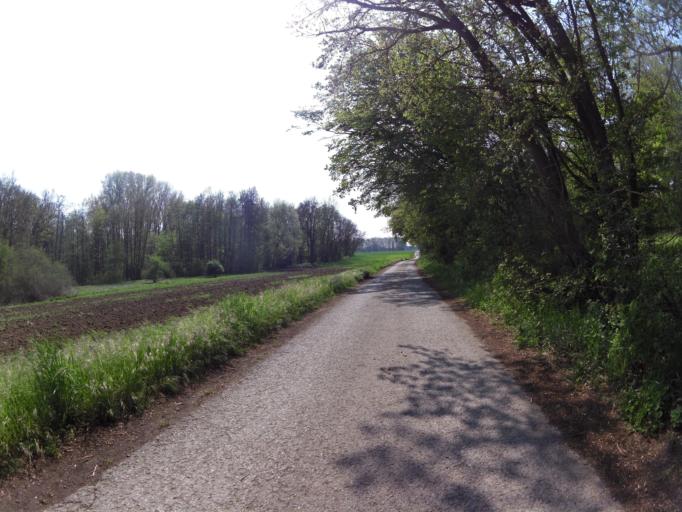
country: DE
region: Bavaria
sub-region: Regierungsbezirk Unterfranken
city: Ochsenfurt
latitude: 49.7046
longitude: 10.0670
